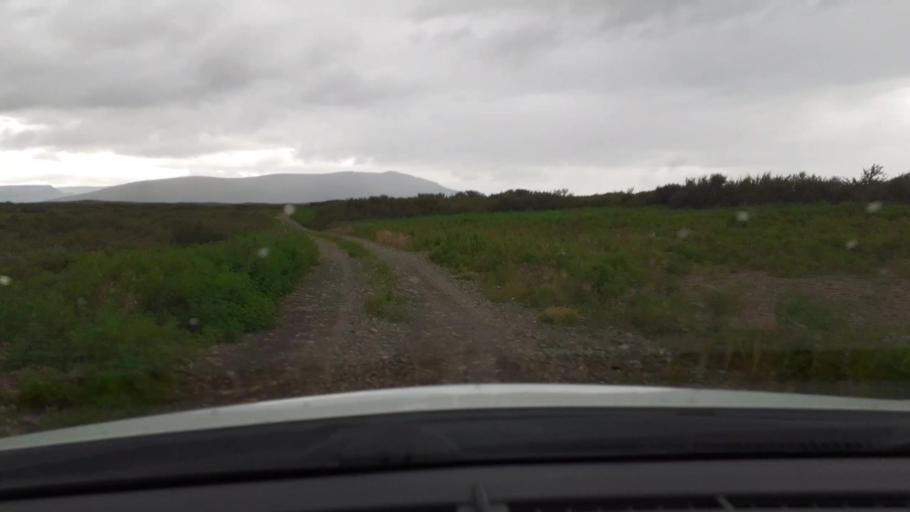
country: IS
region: West
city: Borgarnes
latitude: 64.4563
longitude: -21.9519
